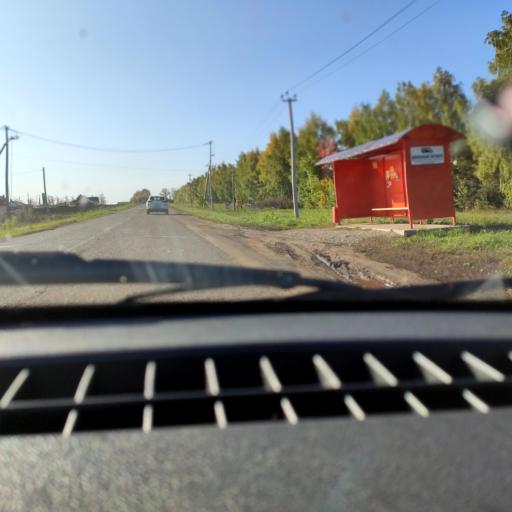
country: RU
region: Bashkortostan
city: Avdon
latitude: 54.5955
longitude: 55.7998
